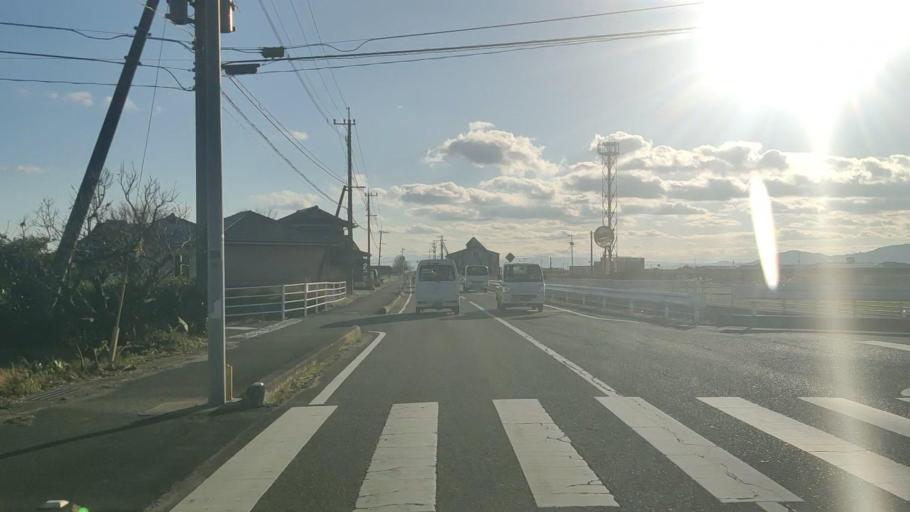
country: JP
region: Saga Prefecture
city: Saga-shi
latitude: 33.2876
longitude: 130.2336
